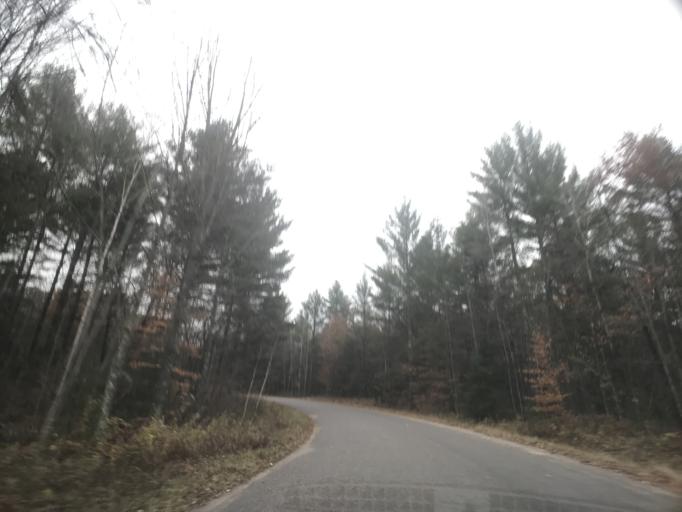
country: US
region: Wisconsin
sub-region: Oconto County
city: Gillett
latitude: 45.3732
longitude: -88.3198
